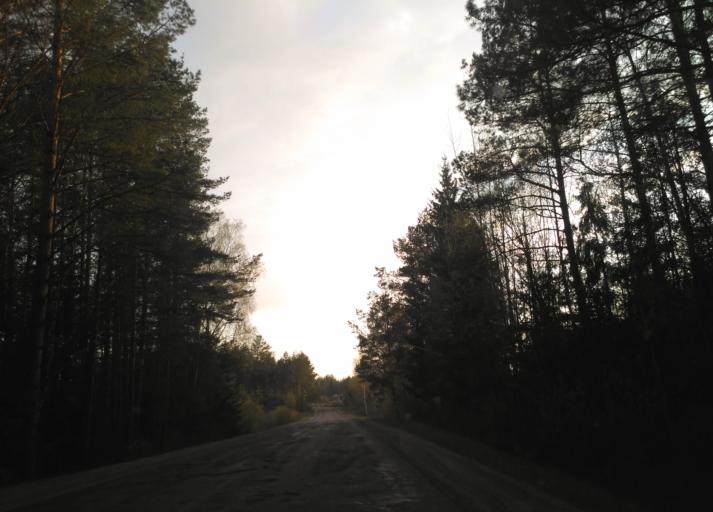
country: BY
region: Minsk
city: Loshnitsa
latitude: 54.4196
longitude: 28.6432
